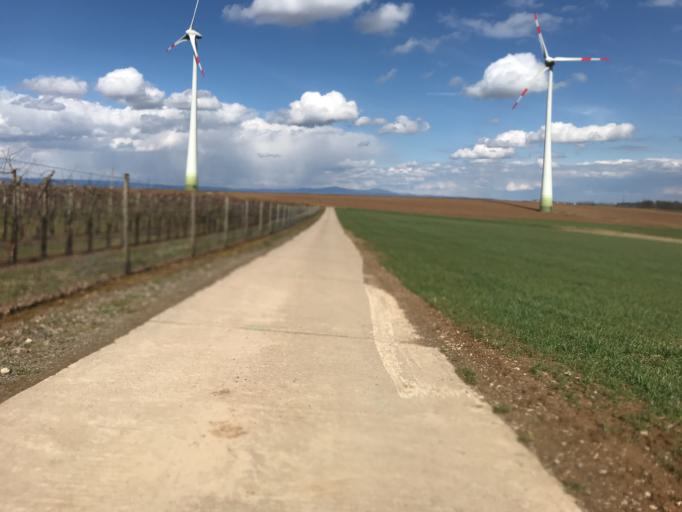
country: DE
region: Rheinland-Pfalz
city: Klein-Winternheim
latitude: 49.9357
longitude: 8.2399
